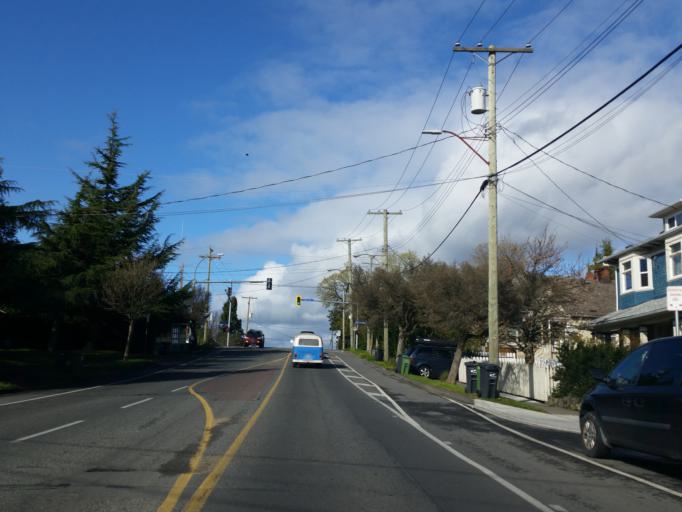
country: CA
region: British Columbia
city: Victoria
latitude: 48.4357
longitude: -123.3836
